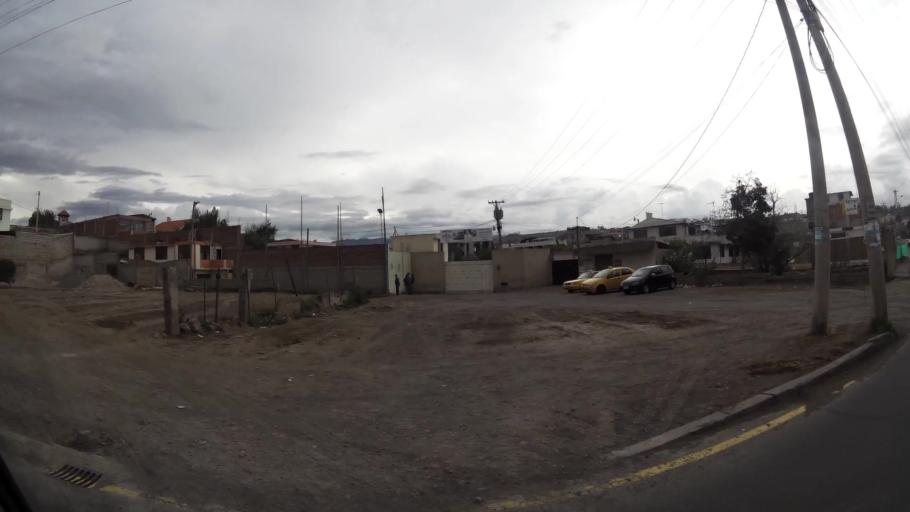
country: EC
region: Tungurahua
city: Ambato
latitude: -1.2762
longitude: -78.6262
